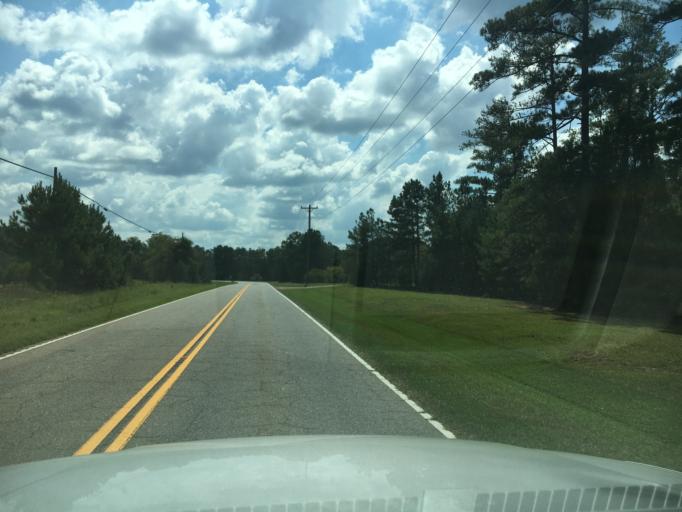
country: US
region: South Carolina
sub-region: Greenwood County
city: Greenwood
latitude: 34.1094
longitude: -82.1302
